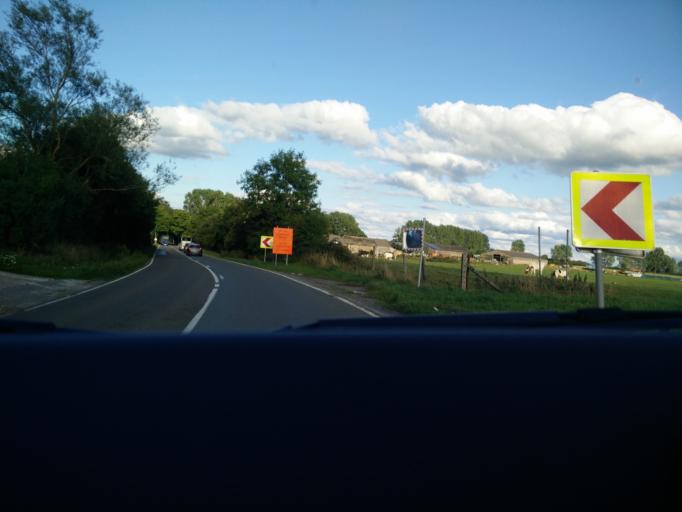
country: BE
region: Wallonia
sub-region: Province de Namur
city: Philippeville
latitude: 50.1943
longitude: 4.5161
